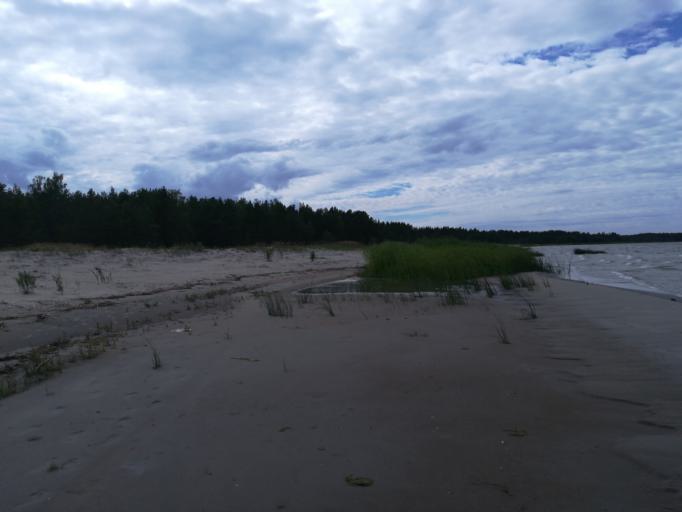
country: RU
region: Leningrad
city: Ust'-Luga
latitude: 59.6787
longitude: 28.2435
